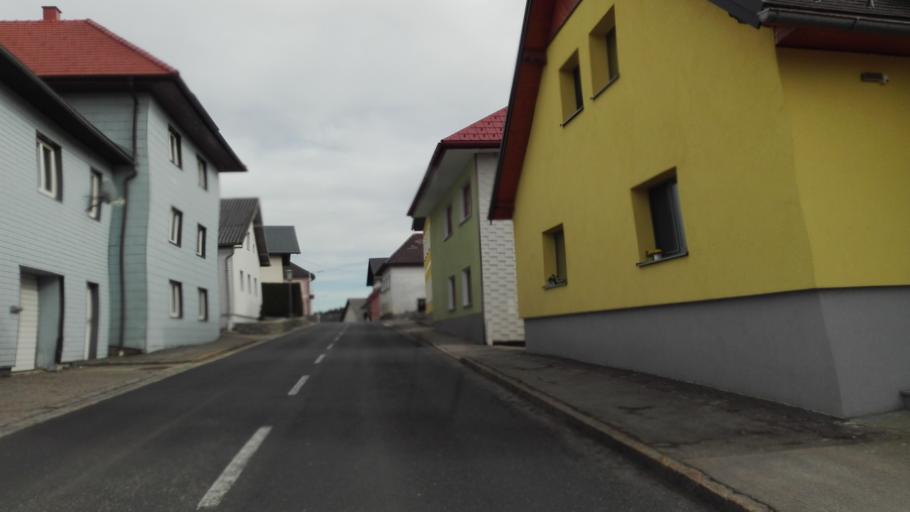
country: AT
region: Upper Austria
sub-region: Politischer Bezirk Rohrbach
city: Nebelberg
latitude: 48.6074
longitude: 13.8360
